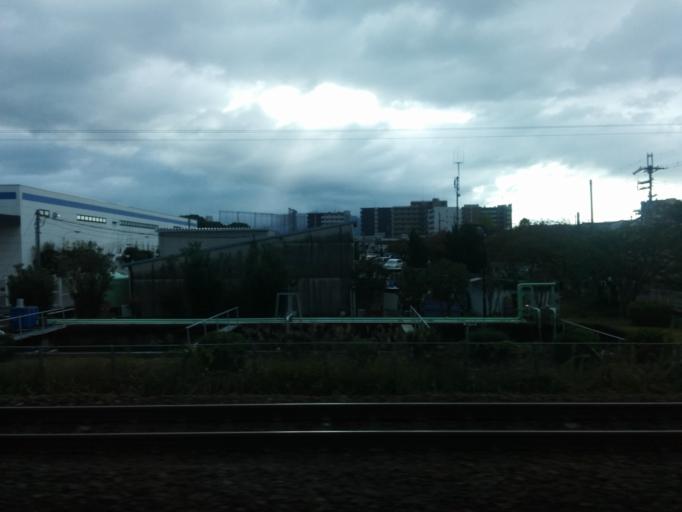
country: JP
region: Shiga Prefecture
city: Kusatsu
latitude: 35.0068
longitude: 135.9496
